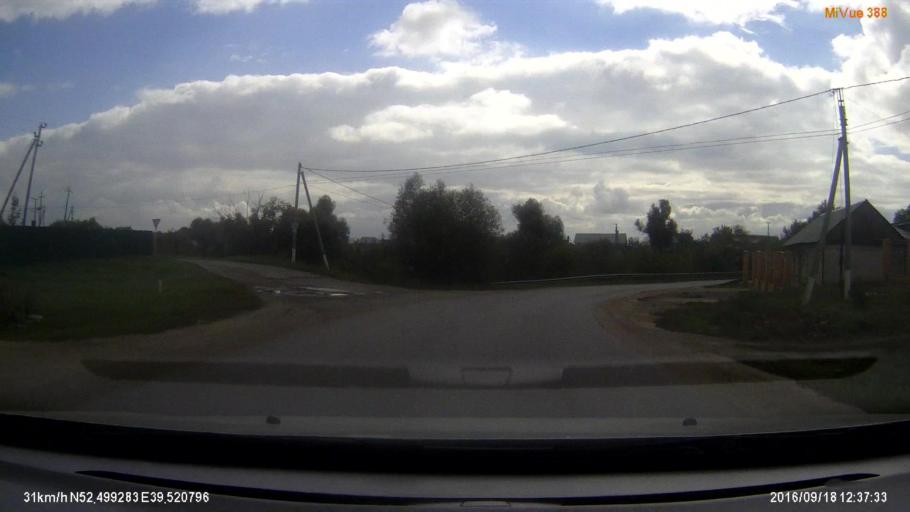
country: RU
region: Lipetsk
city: Syrskoye
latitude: 52.4990
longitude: 39.5209
